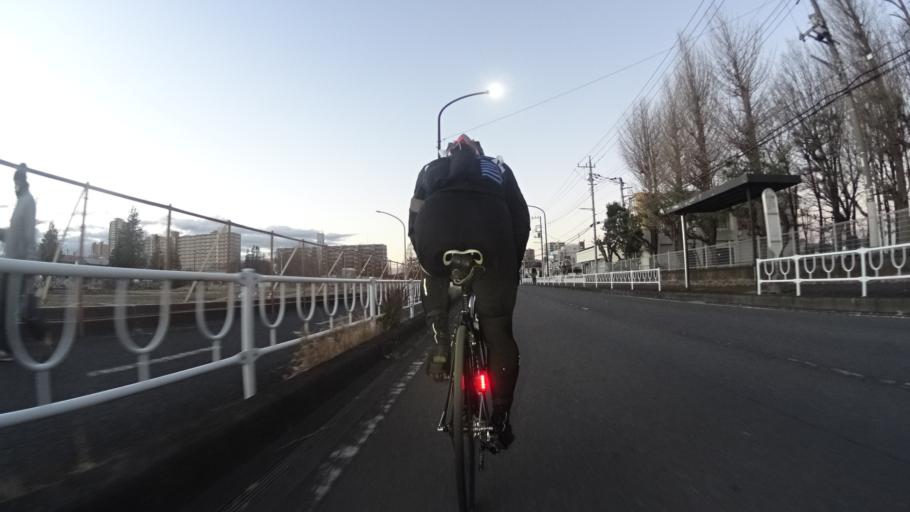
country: JP
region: Tokyo
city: Hachioji
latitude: 35.5855
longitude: 139.3679
